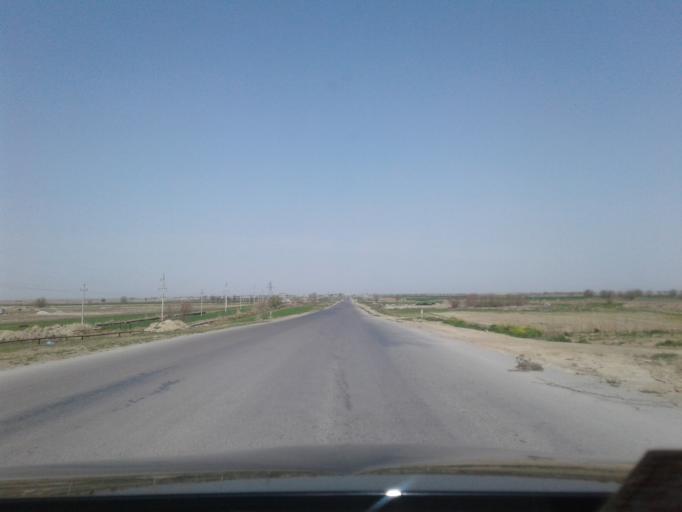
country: TM
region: Ahal
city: Abadan
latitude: 38.1915
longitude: 57.9730
